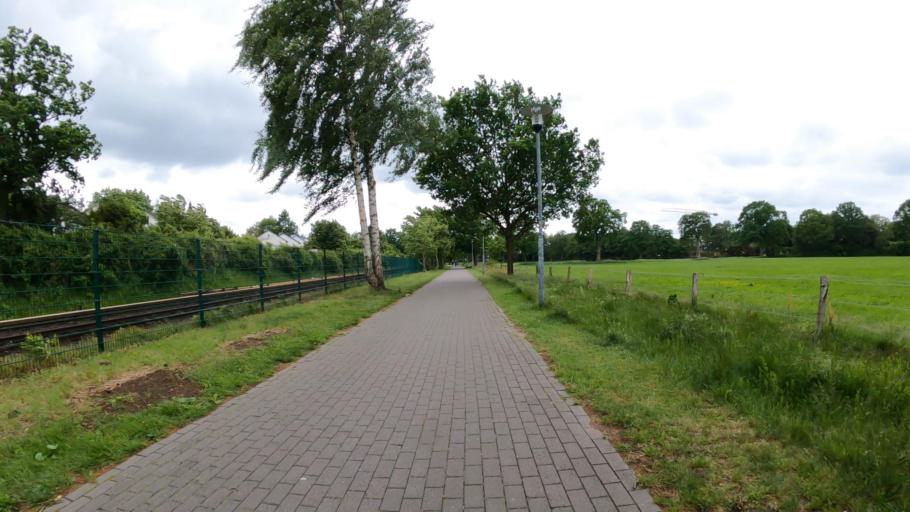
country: DE
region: Schleswig-Holstein
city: Norderstedt
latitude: 53.6944
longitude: 9.9879
